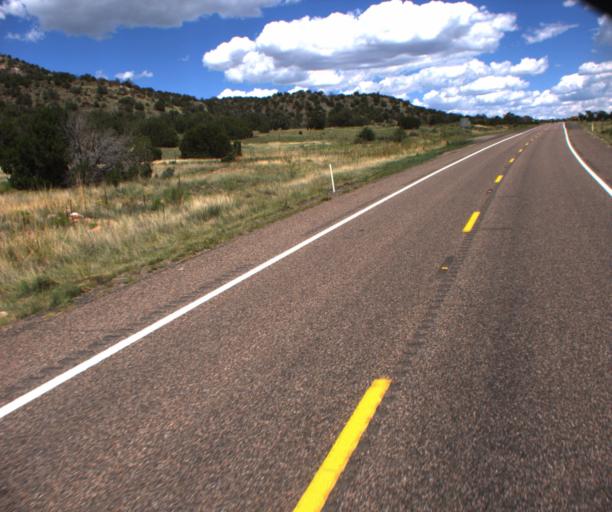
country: US
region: Arizona
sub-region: Apache County
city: Springerville
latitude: 34.1669
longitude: -109.0481
